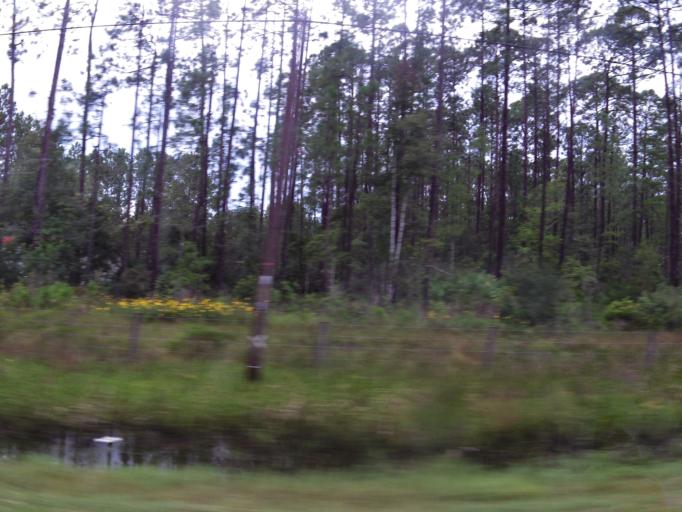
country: US
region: Florida
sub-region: Duval County
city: Baldwin
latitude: 30.3445
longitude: -81.9093
